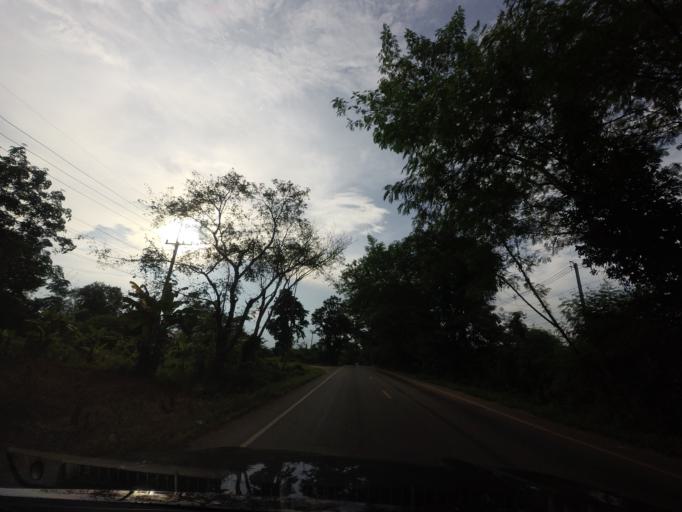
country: TH
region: Nong Khai
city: Pho Tak
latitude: 17.7843
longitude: 102.3733
